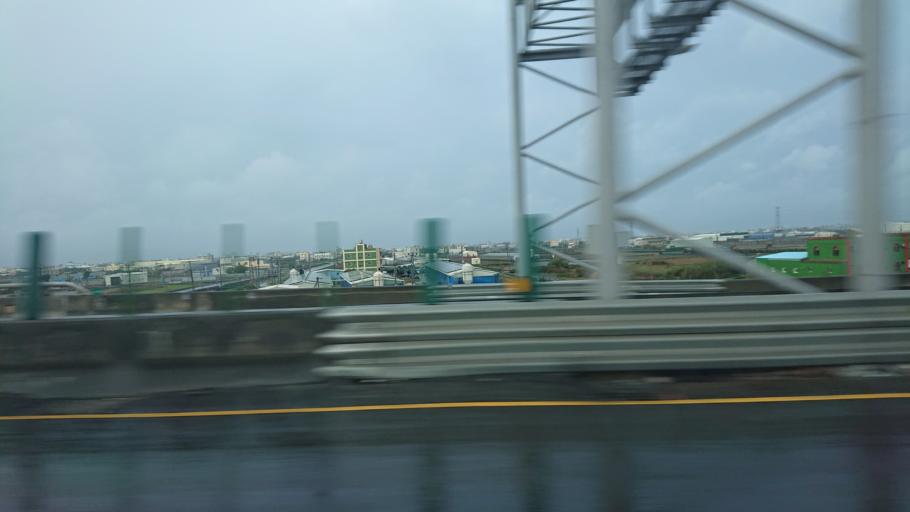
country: TW
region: Taiwan
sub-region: Changhua
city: Chang-hua
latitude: 24.1330
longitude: 120.4401
